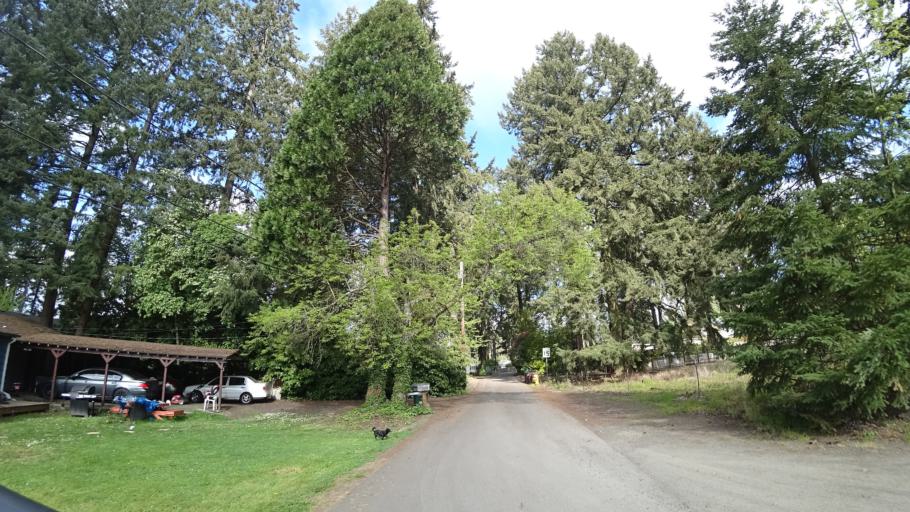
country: US
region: Oregon
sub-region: Washington County
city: Hillsboro
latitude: 45.5128
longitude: -122.9776
